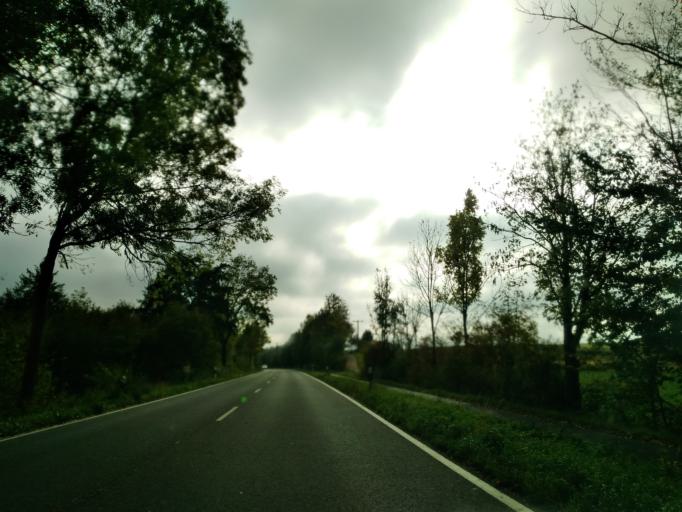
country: DE
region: North Rhine-Westphalia
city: Sankt Augustin
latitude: 50.7423
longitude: 7.2185
